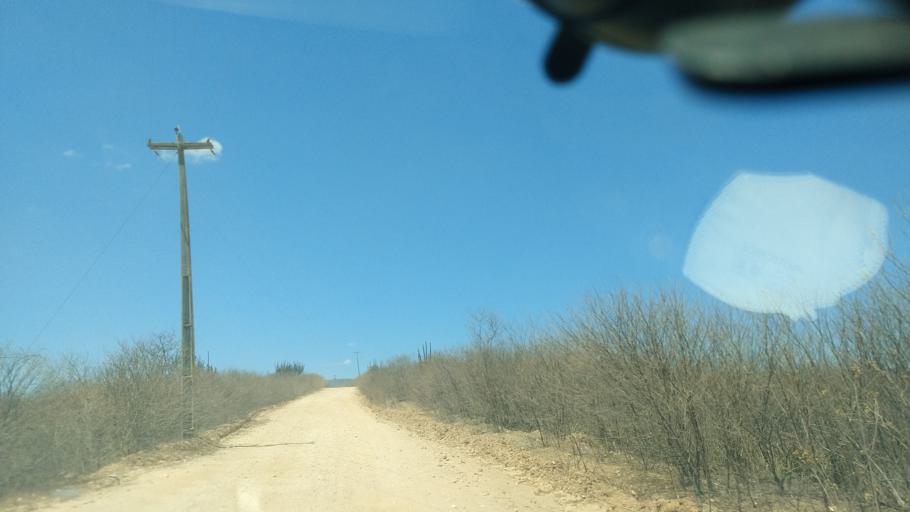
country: BR
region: Rio Grande do Norte
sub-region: Cerro Cora
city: Cerro Cora
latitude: -6.0105
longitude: -36.2894
